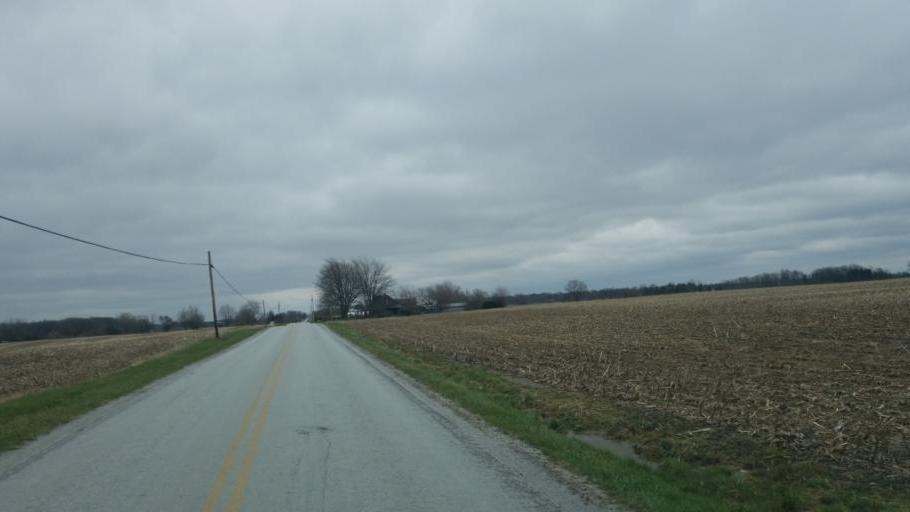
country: US
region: Ohio
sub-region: Hardin County
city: Kenton
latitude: 40.6588
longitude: -83.5714
